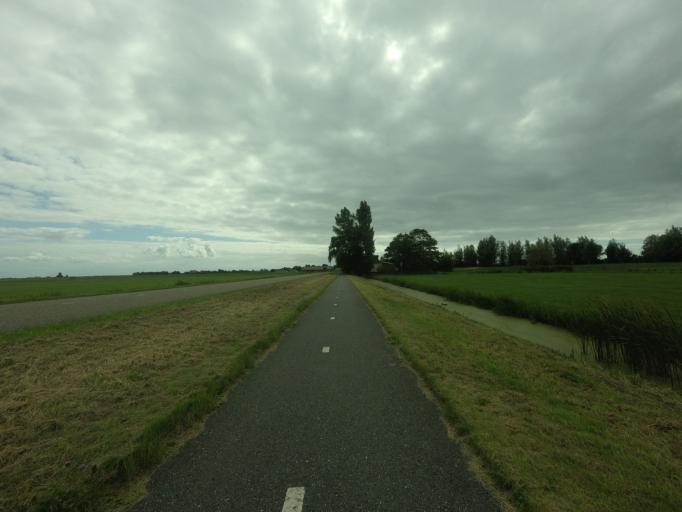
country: NL
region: Friesland
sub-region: Sudwest Fryslan
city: Heeg
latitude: 52.9770
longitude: 5.5422
